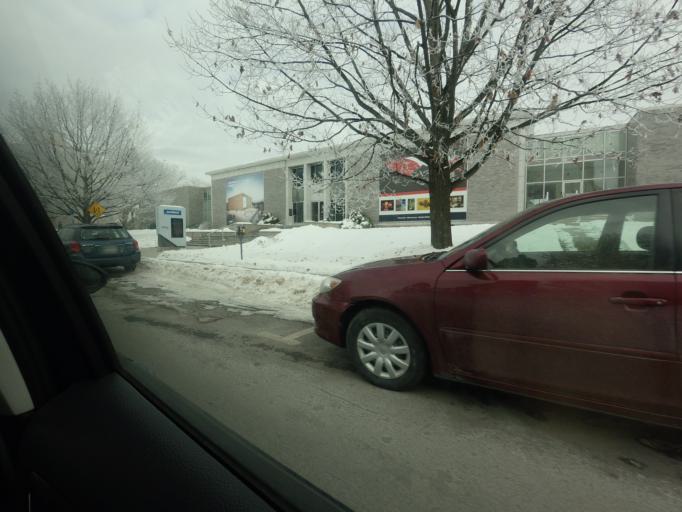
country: CA
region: New Brunswick
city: Fredericton
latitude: 45.9597
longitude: -66.6357
